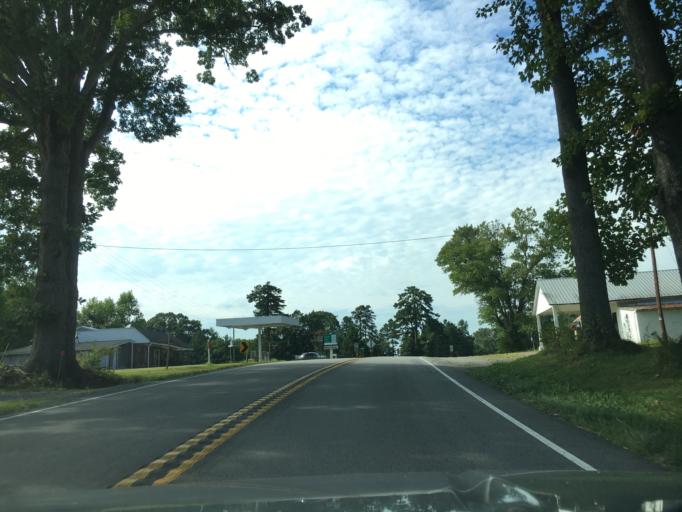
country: US
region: Virginia
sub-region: Halifax County
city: Mountain Road
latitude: 36.8757
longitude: -79.0150
